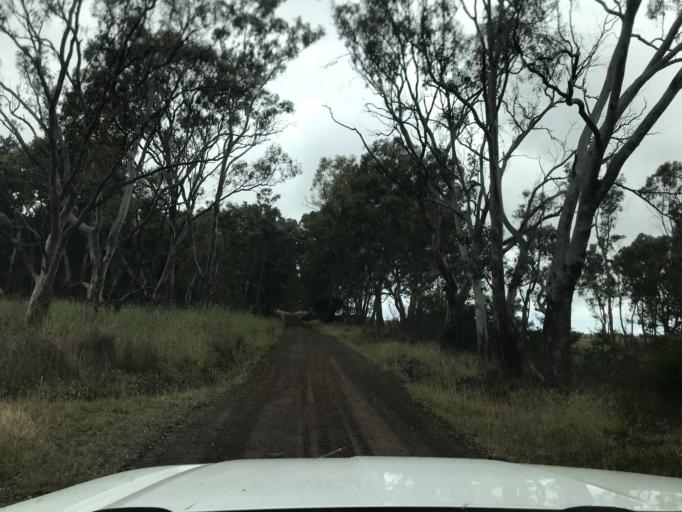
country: AU
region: South Australia
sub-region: Wattle Range
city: Penola
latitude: -37.2345
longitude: 141.4381
